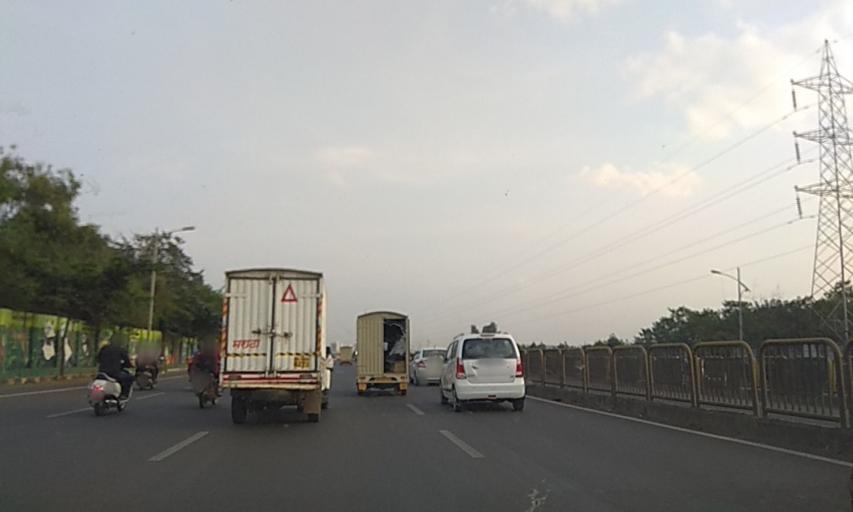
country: IN
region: Maharashtra
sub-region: Pune Division
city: Pimpri
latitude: 18.5802
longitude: 73.7998
